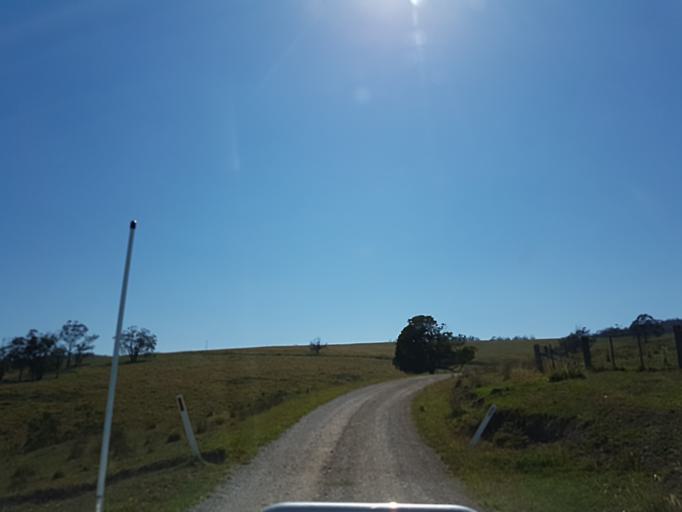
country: AU
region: Victoria
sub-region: East Gippsland
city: Lakes Entrance
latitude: -37.2345
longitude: 148.2658
